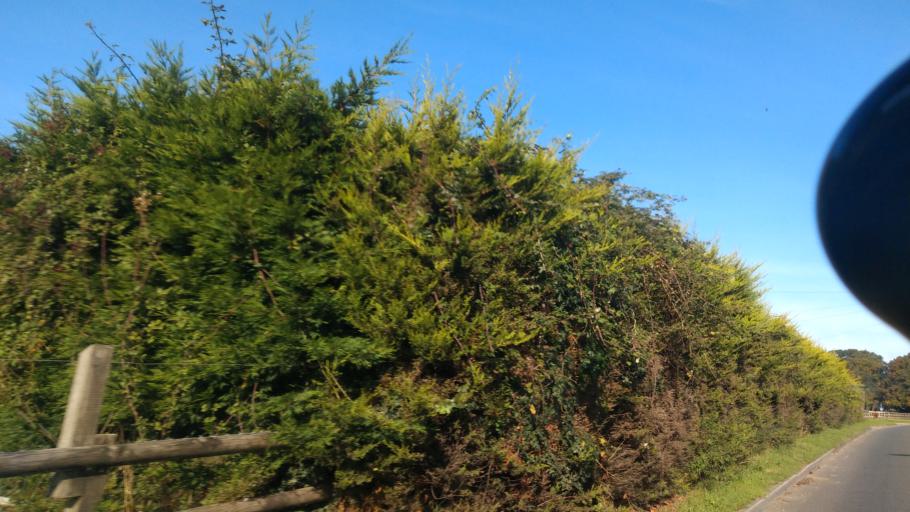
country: GB
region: England
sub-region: Hampshire
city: Lee-on-the-Solent
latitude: 50.8366
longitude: -1.2228
